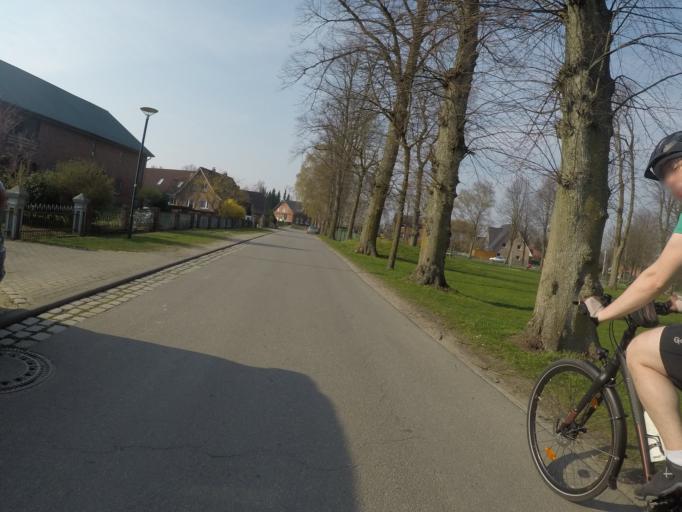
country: DE
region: Schleswig-Holstein
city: Leezen
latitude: 53.8699
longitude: 10.2473
